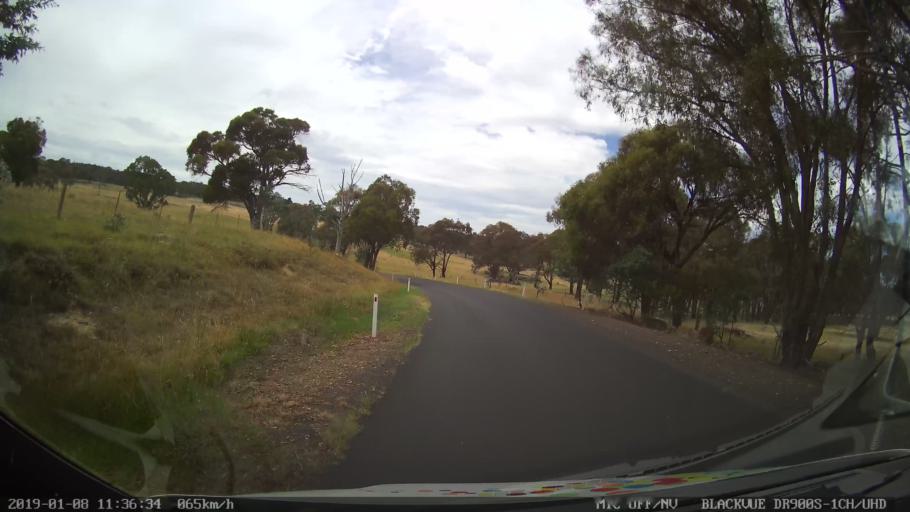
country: AU
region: New South Wales
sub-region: Guyra
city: Guyra
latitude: -30.3464
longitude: 151.5448
